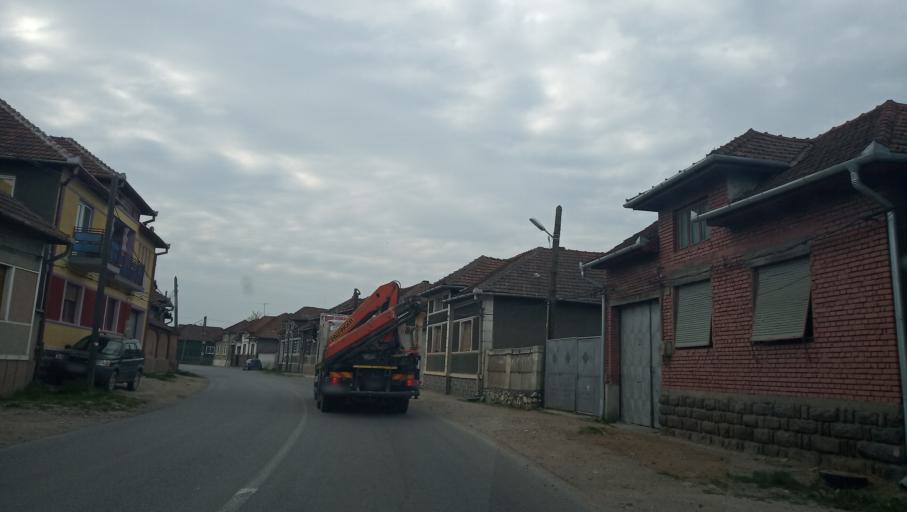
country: RO
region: Bihor
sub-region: Comuna Lunca
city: Lunca
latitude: 46.5197
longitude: 22.4639
